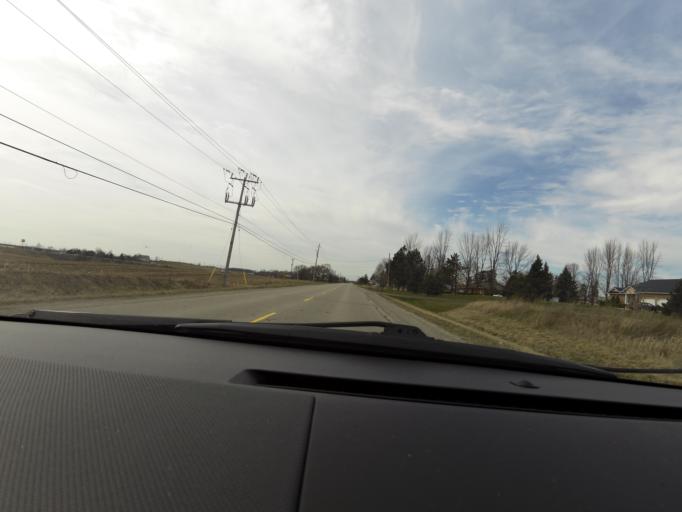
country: CA
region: Ontario
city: Ancaster
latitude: 43.0878
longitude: -79.9374
